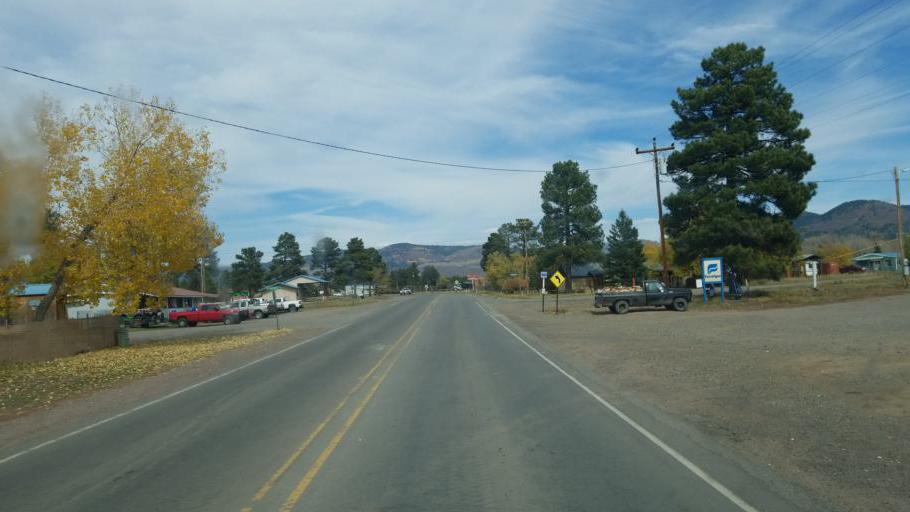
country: US
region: New Mexico
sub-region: Rio Arriba County
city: Chama
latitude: 36.8940
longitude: -106.5820
